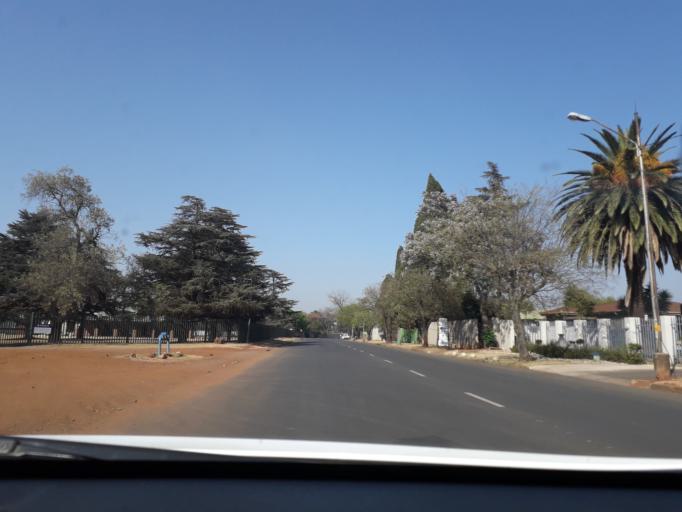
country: ZA
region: Gauteng
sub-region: City of Johannesburg Metropolitan Municipality
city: Modderfontein
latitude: -26.0982
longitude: 28.2405
